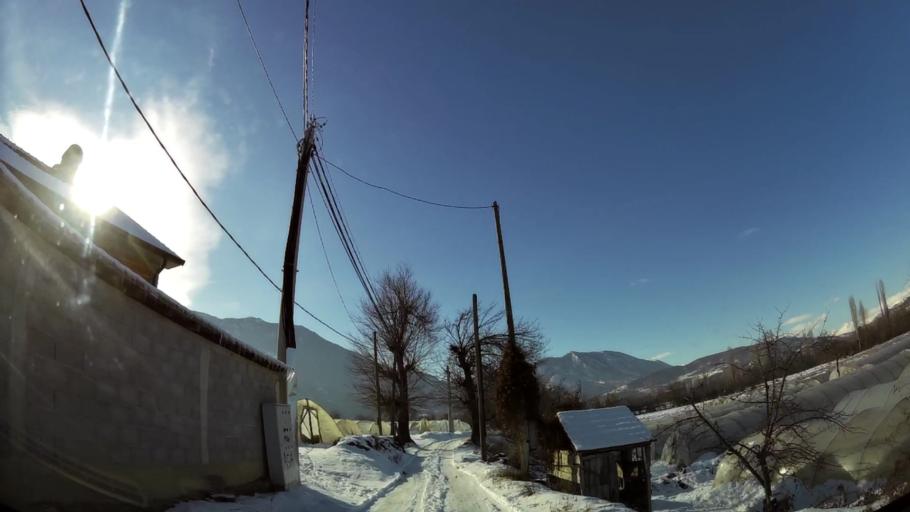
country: MK
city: Grchec
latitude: 41.9877
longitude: 21.3258
